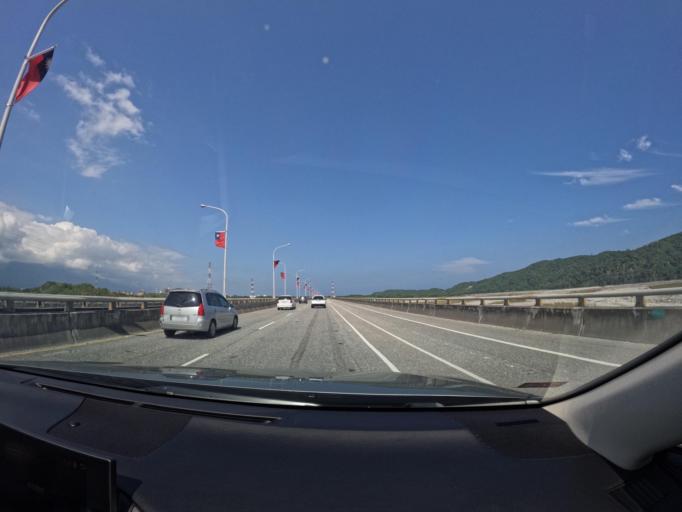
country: TW
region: Taiwan
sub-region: Hualien
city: Hualian
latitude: 23.9150
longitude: 121.5805
